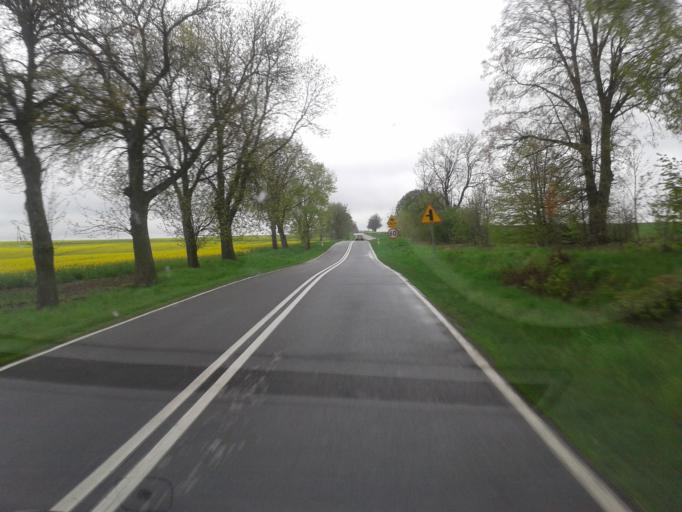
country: PL
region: Lublin Voivodeship
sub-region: Powiat tomaszowski
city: Telatyn
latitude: 50.5516
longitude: 23.9326
